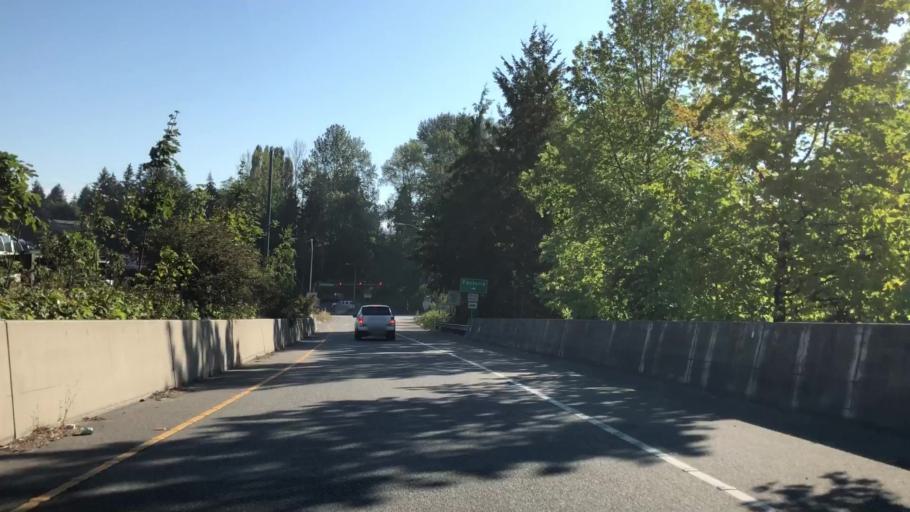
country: US
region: Washington
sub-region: King County
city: Newport
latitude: 47.5667
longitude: -122.1809
